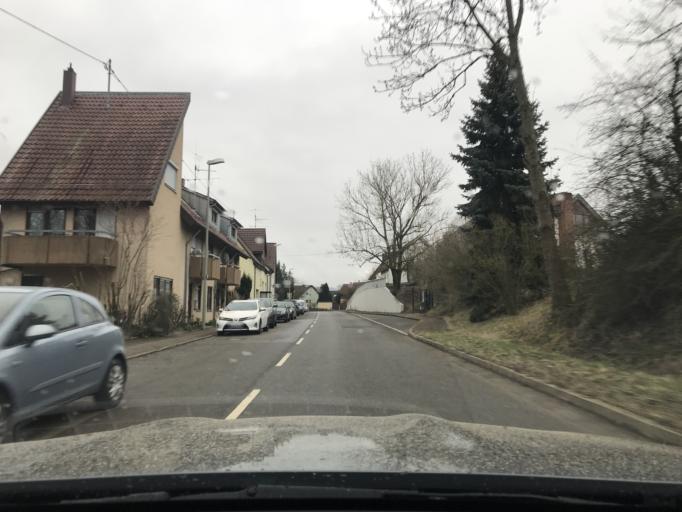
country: DE
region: Baden-Wuerttemberg
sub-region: Regierungsbezirk Stuttgart
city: Affalterbach
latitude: 48.8895
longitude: 9.3104
